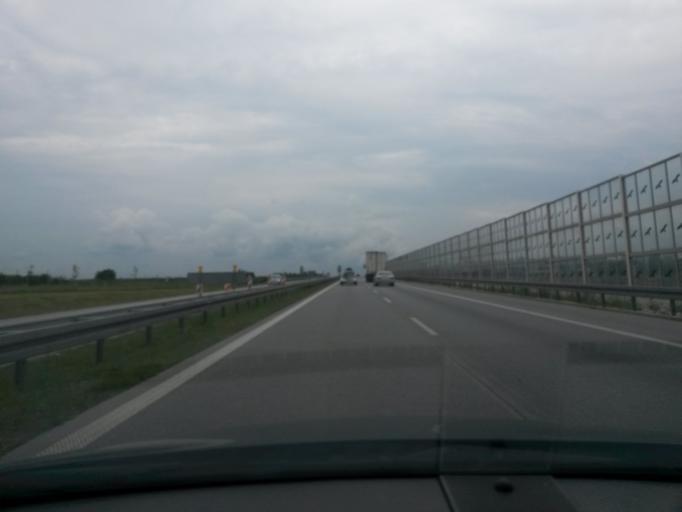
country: PL
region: Lodz Voivodeship
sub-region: Powiat skierniewicki
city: Kowiesy
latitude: 51.9137
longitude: 20.4488
